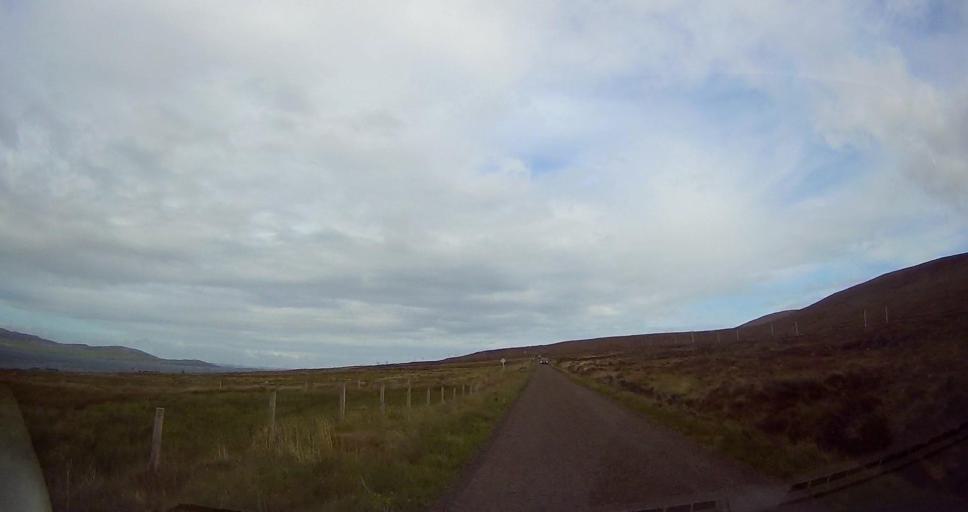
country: GB
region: Scotland
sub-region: Orkney Islands
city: Stromness
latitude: 58.9029
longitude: -3.2993
